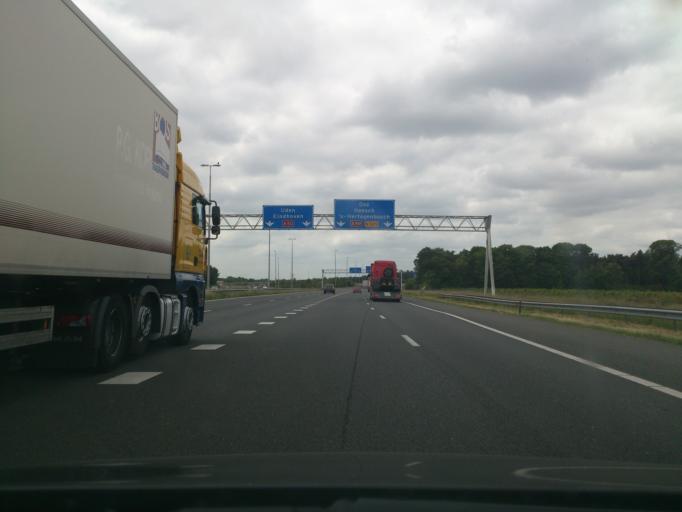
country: NL
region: North Brabant
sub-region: Gemeente Oss
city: Berghem
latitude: 51.7430
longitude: 5.5890
